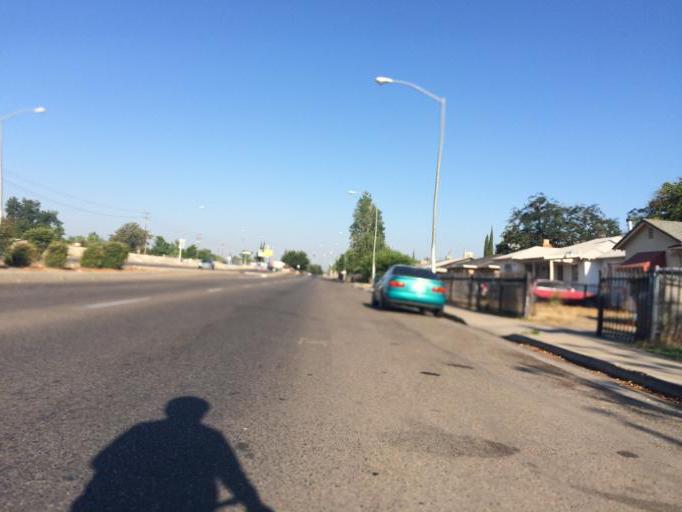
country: US
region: California
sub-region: Fresno County
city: Fresno
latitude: 36.7651
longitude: -119.7612
